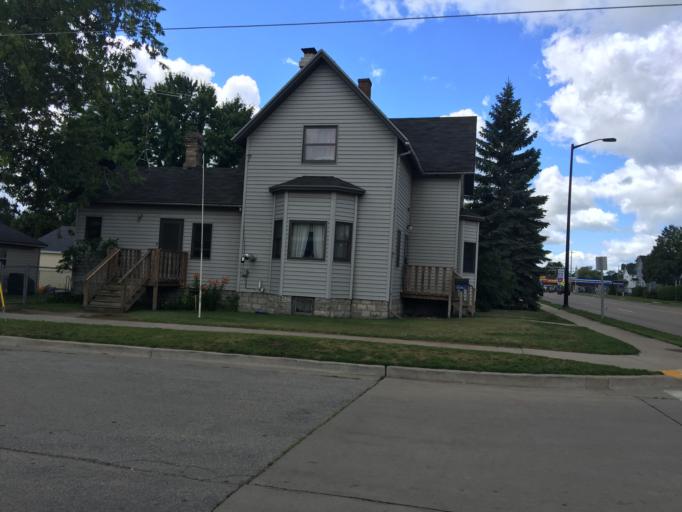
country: US
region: Wisconsin
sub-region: Marinette County
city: Marinette
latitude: 45.0972
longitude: -87.6417
